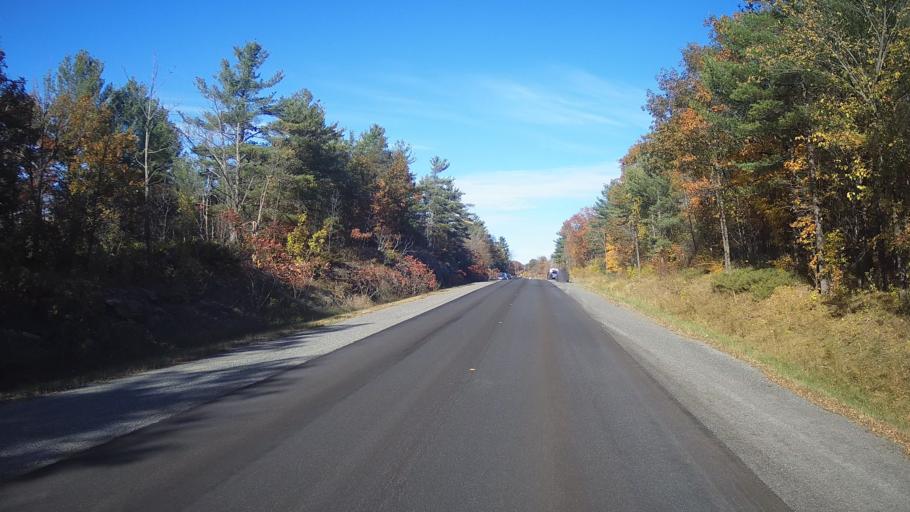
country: CA
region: Ontario
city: Kingston
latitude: 44.5032
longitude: -76.4751
